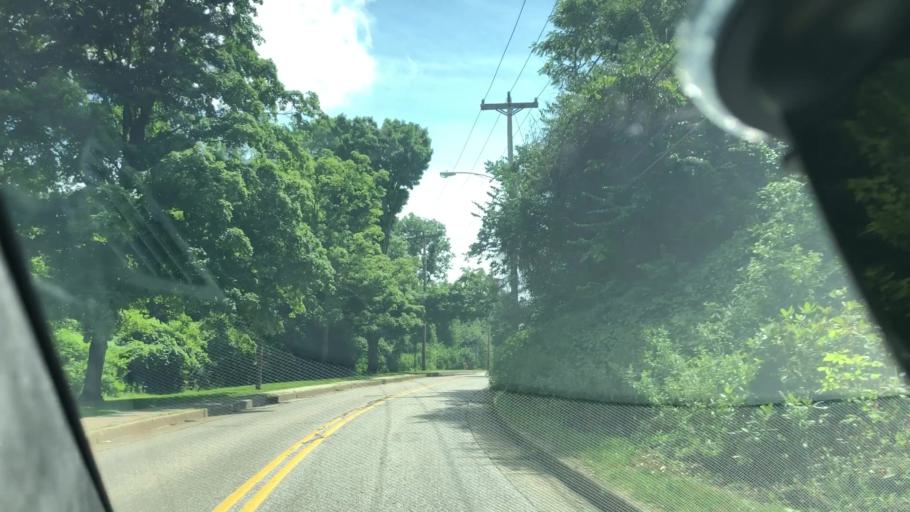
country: US
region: Pennsylvania
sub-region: Allegheny County
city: Mount Lebanon
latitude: 40.3680
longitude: -80.0561
